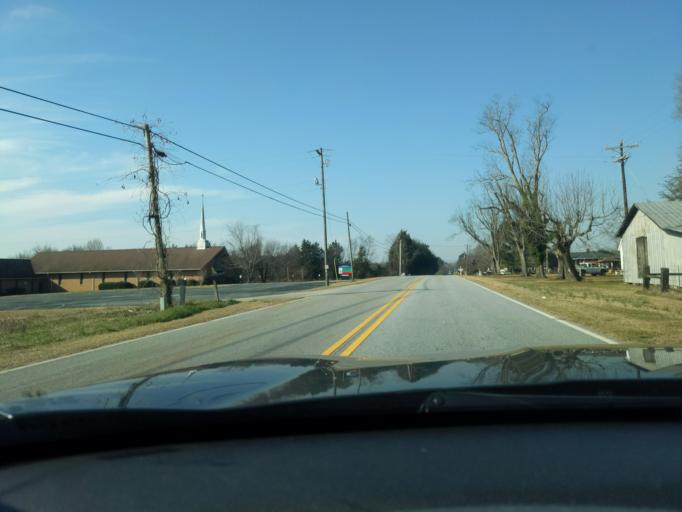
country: US
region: South Carolina
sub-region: Abbeville County
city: Calhoun Falls
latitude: 34.0931
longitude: -82.5751
